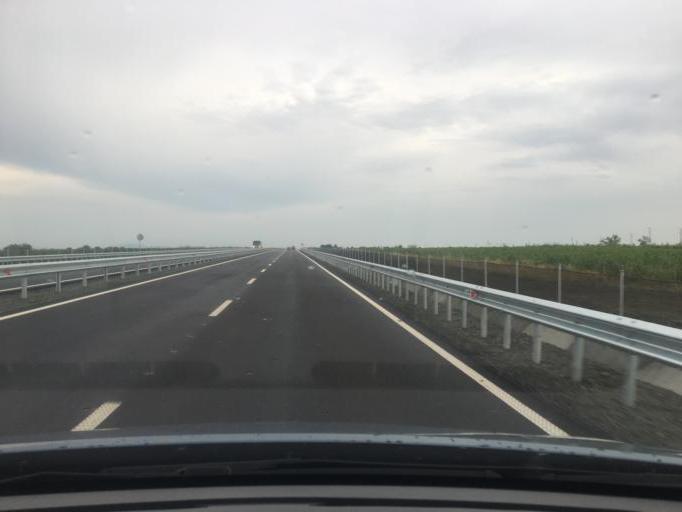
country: BG
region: Burgas
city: Aheloy
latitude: 42.6059
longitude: 27.6202
